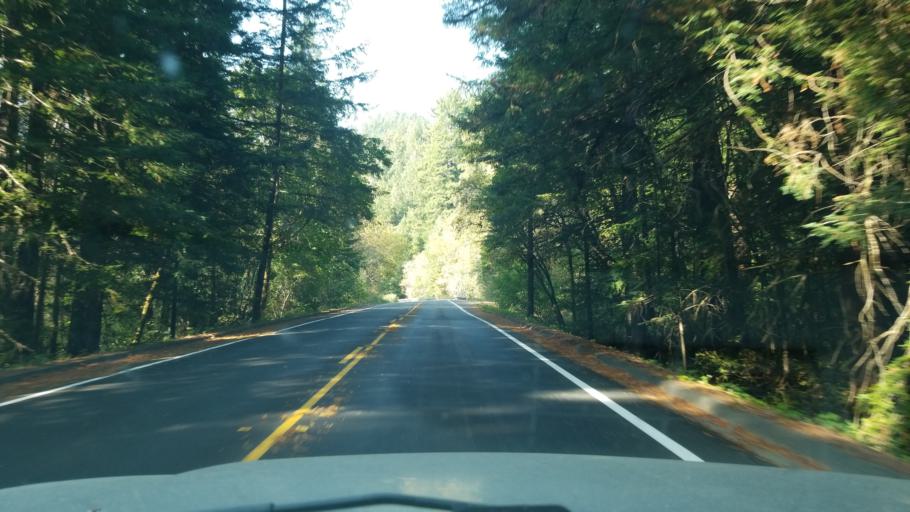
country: US
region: California
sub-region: Humboldt County
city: Redway
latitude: 40.2181
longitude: -123.7862
